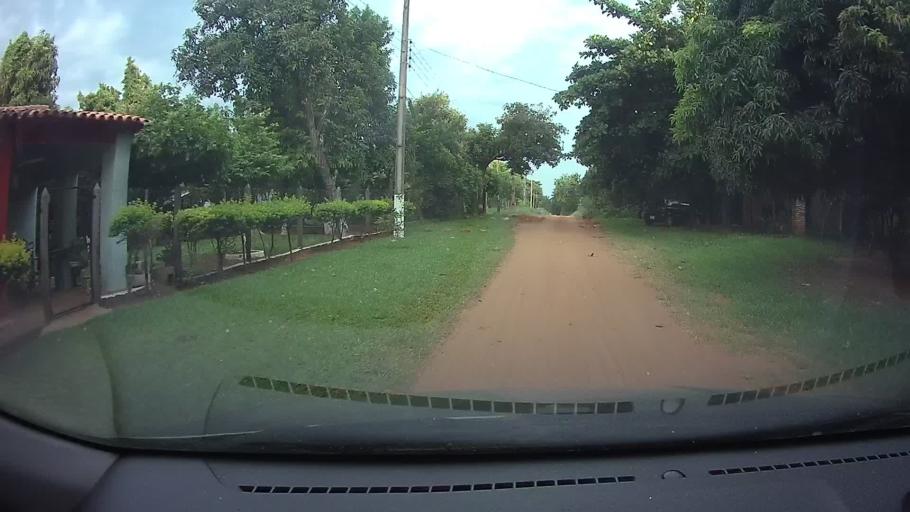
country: PY
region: Central
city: Limpio
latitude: -25.2436
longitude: -57.4533
